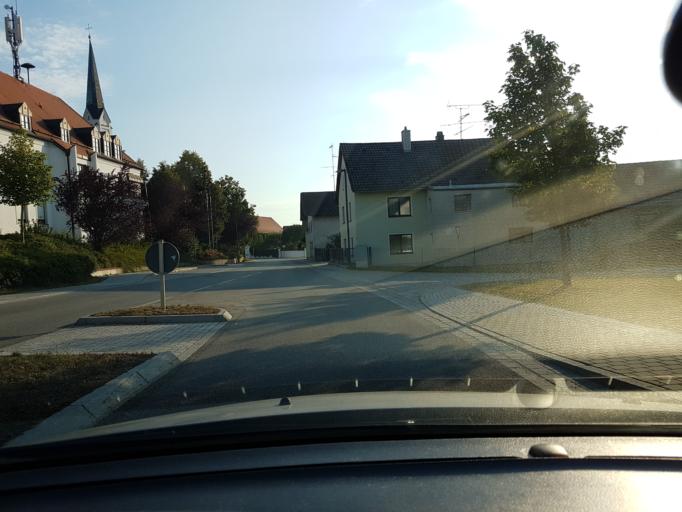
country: DE
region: Bavaria
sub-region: Lower Bavaria
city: Gerzen
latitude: 48.5054
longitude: 12.4254
